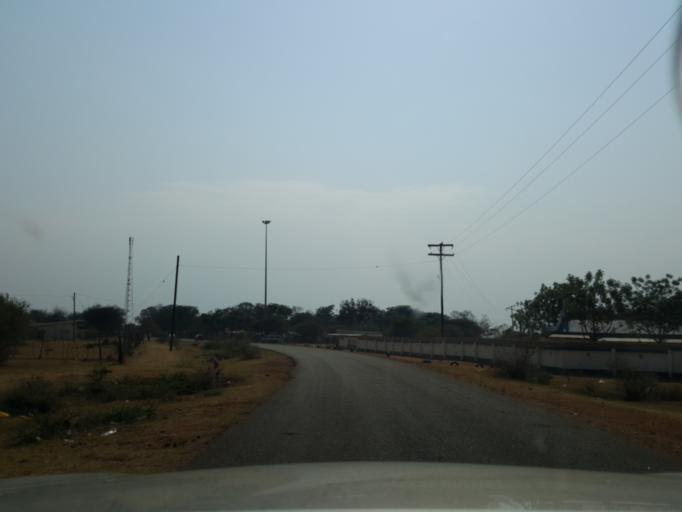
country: BW
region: South East
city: Lobatse
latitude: -25.2868
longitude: 25.9116
